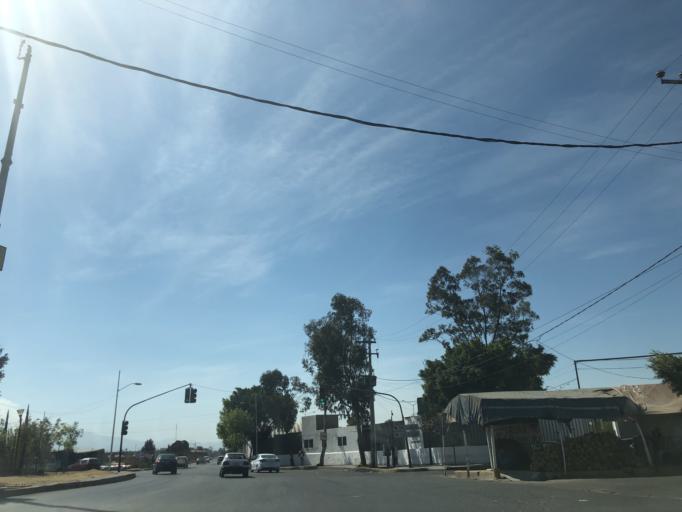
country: MX
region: Mexico
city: Ciudad Nezahualcoyotl
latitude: 19.3833
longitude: -99.0392
